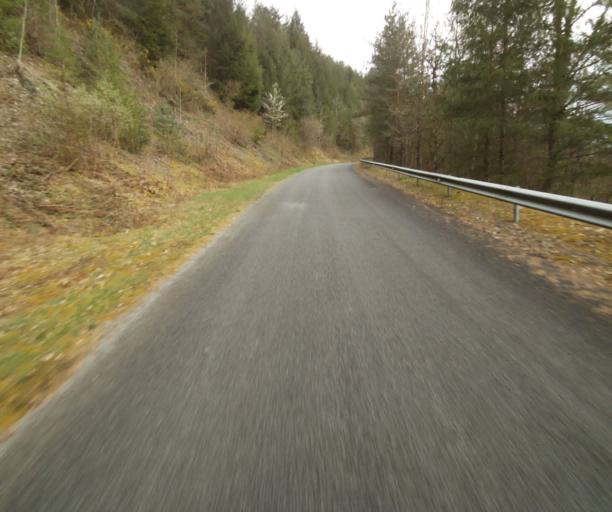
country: FR
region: Limousin
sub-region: Departement de la Correze
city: Laguenne
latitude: 45.2502
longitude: 1.7755
